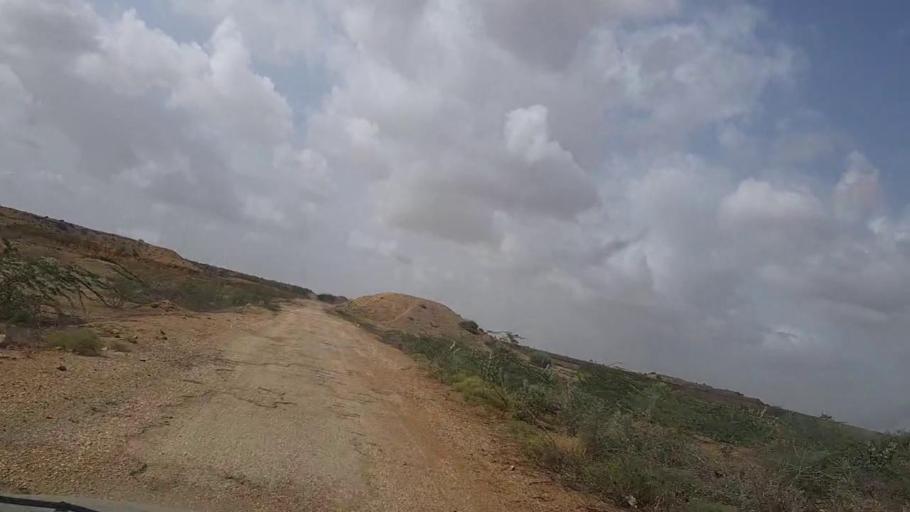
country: PK
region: Sindh
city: Thatta
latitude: 24.8851
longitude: 67.8963
